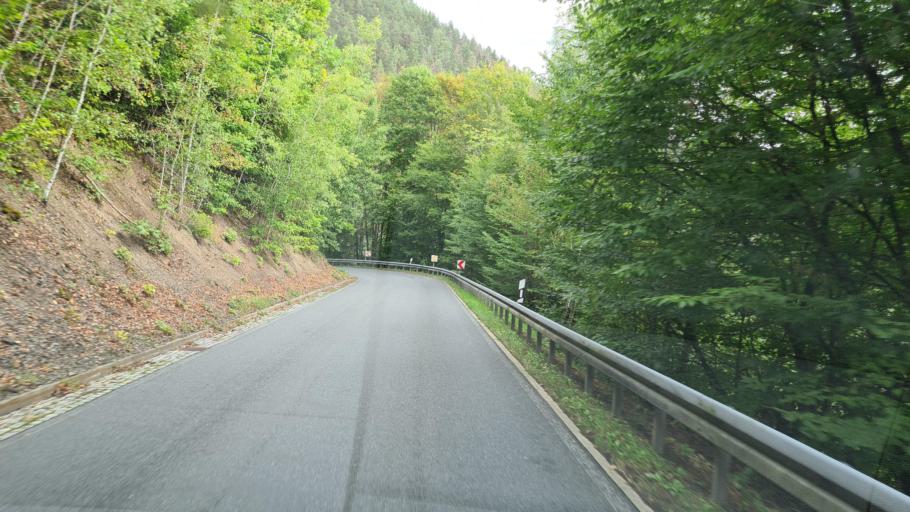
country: DE
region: Thuringia
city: Leutenberg
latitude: 50.5640
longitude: 11.4373
